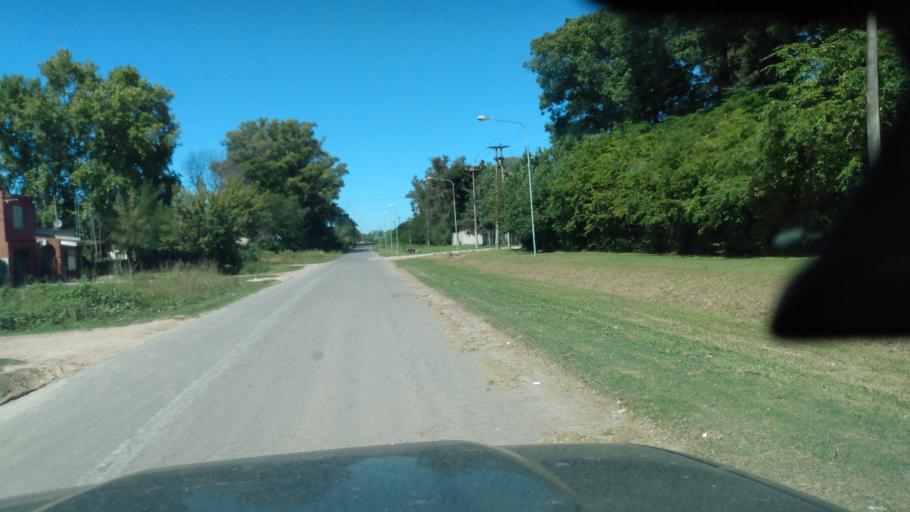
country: AR
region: Buenos Aires
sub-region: Partido de Lujan
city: Lujan
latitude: -34.5717
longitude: -59.1304
